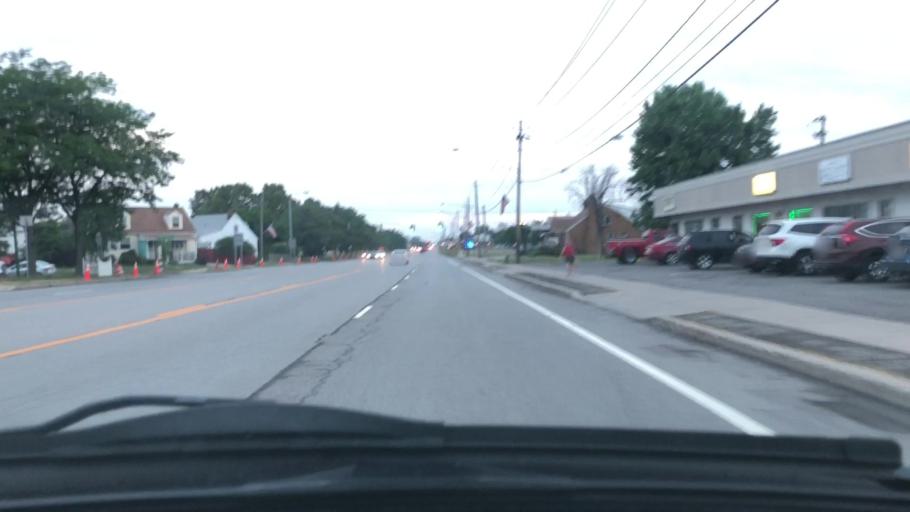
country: US
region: New York
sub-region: Erie County
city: Sloan
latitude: 42.9120
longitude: -78.7842
